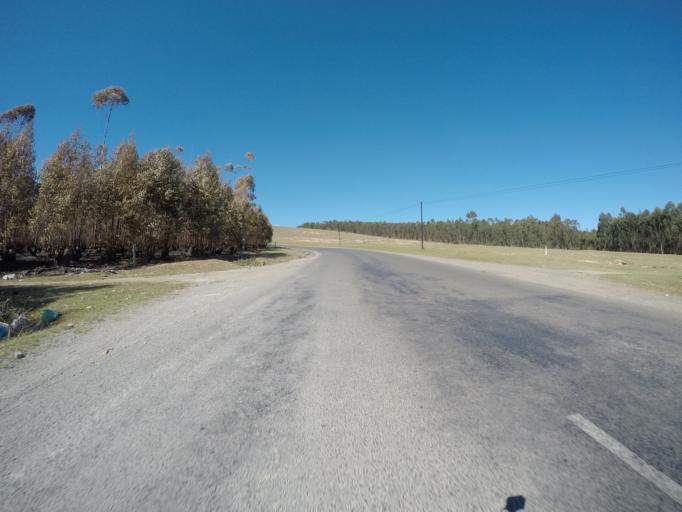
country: ZA
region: Eastern Cape
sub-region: OR Tambo District Municipality
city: Mthatha
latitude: -31.7770
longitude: 28.7375
